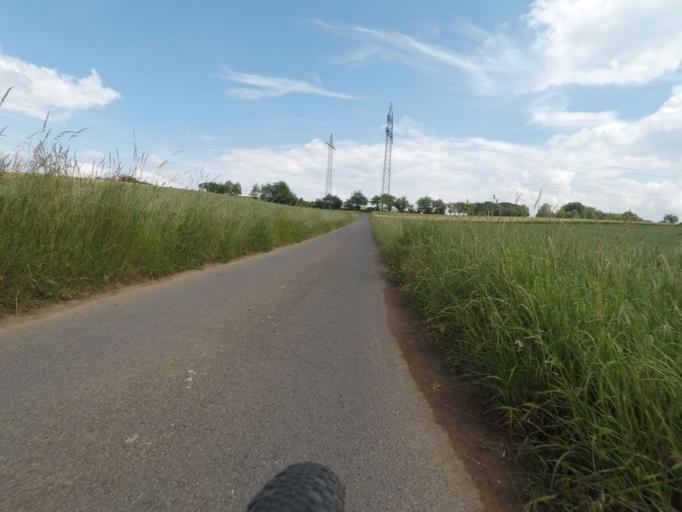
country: DE
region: Hesse
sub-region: Regierungsbezirk Kassel
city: Bad Sooden-Allendorf
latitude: 51.2438
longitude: 9.8998
